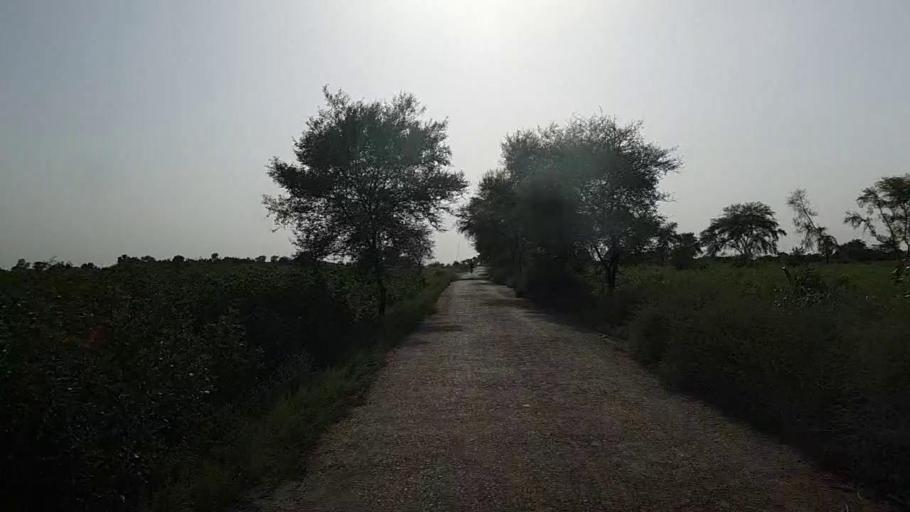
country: PK
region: Sindh
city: Pad Idan
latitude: 26.8531
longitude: 68.3184
